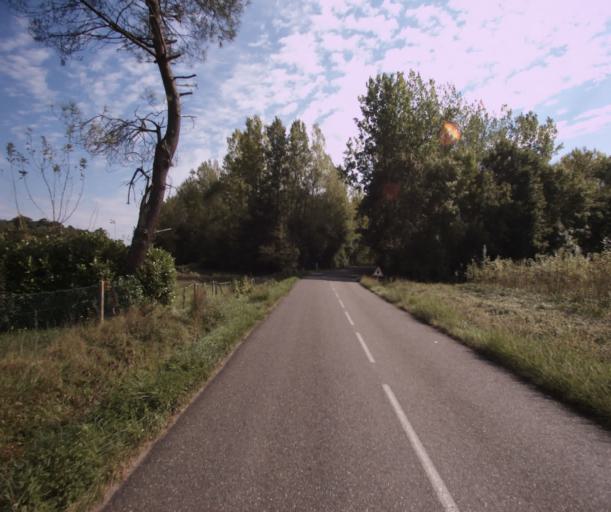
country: FR
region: Midi-Pyrenees
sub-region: Departement du Gers
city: Cazaubon
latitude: 43.9323
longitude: -0.0752
